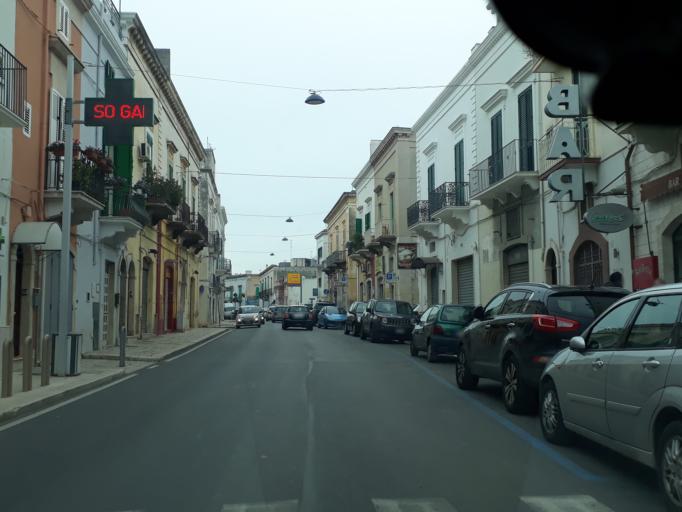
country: IT
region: Apulia
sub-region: Provincia di Brindisi
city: Fasano
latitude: 40.8370
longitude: 17.3608
